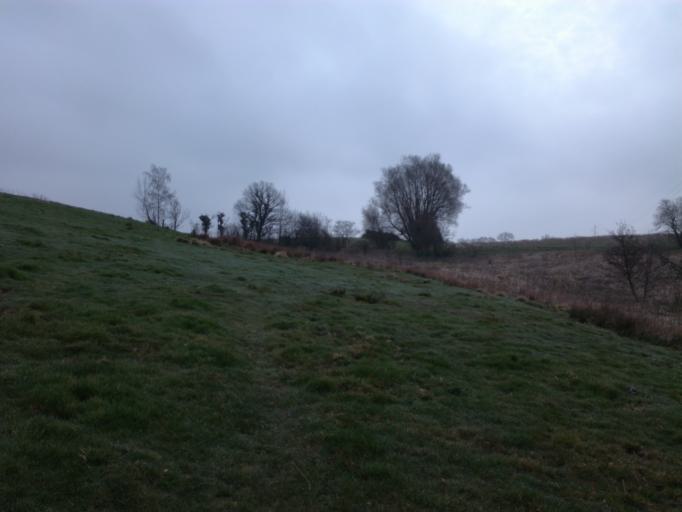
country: DK
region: South Denmark
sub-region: Fredericia Kommune
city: Fredericia
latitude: 55.6132
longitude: 9.7389
